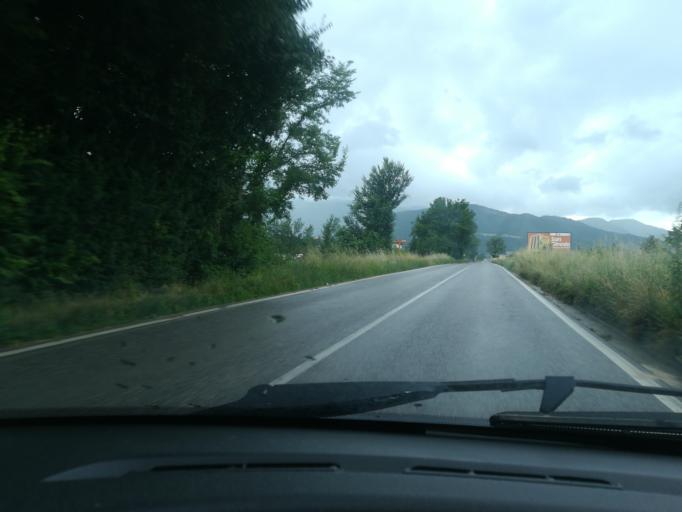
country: IT
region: The Marches
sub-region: Provincia di Macerata
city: San Ginesio
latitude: 43.0825
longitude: 13.2945
